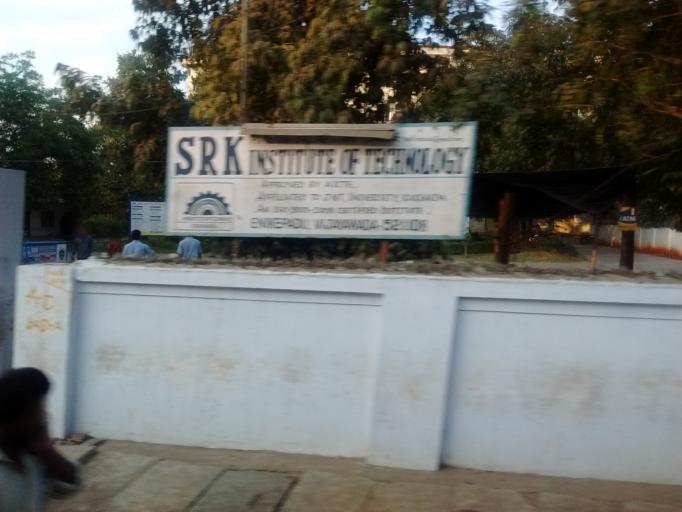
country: IN
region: Andhra Pradesh
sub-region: Krishna
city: Yanamalakuduru
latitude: 16.5170
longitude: 80.6998
